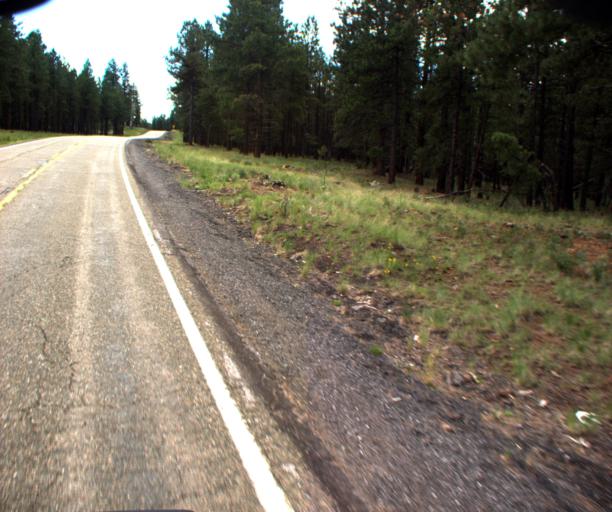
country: US
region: Arizona
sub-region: Coconino County
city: Parks
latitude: 35.3569
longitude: -111.7908
